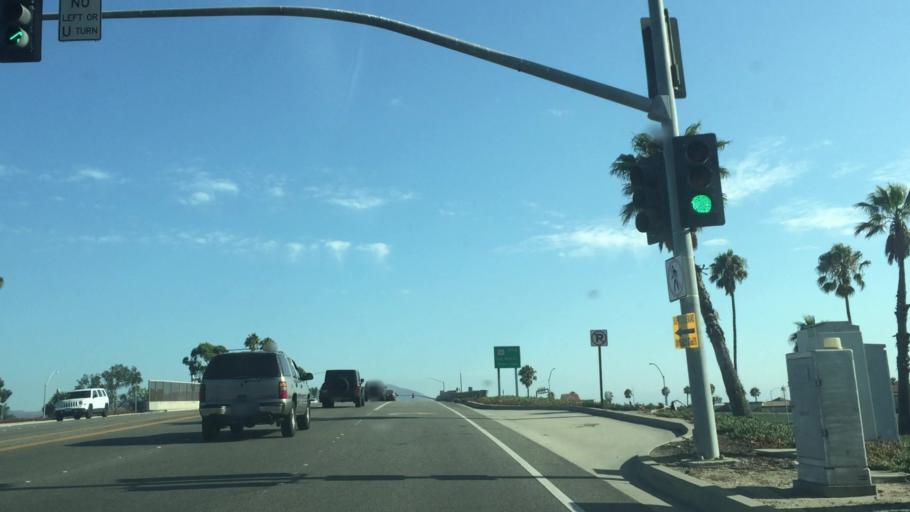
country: US
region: California
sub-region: Ventura County
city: Camarillo
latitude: 34.2203
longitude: -119.0700
